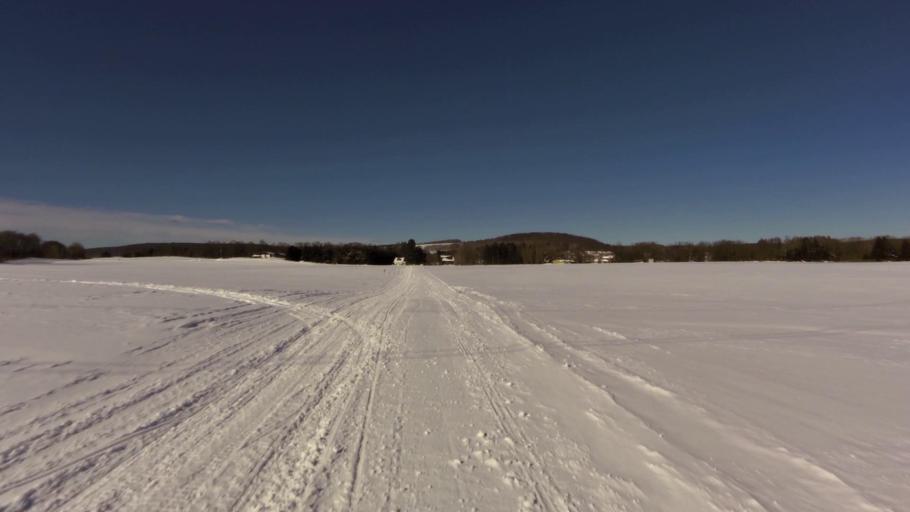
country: US
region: New York
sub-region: Cattaraugus County
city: Delevan
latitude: 42.4075
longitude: -78.5184
